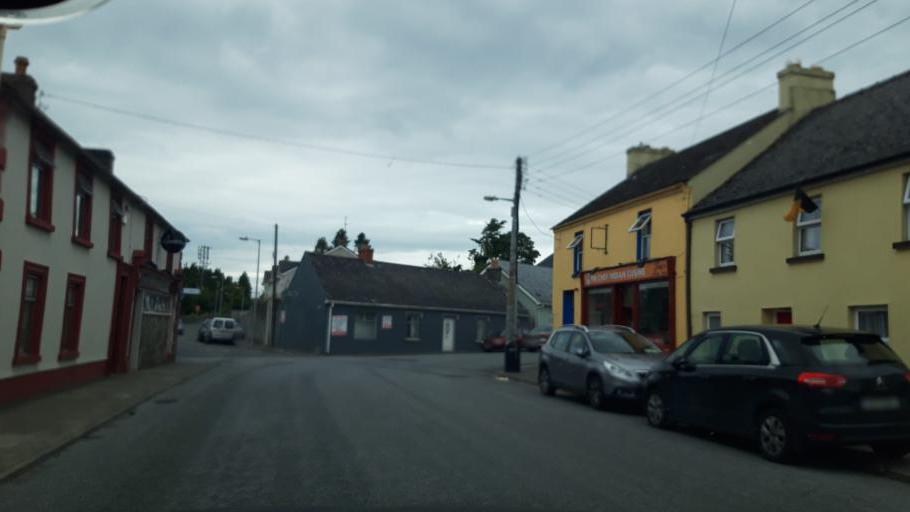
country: IE
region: Leinster
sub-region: Kilkenny
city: Ballyragget
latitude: 52.7896
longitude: -7.3328
